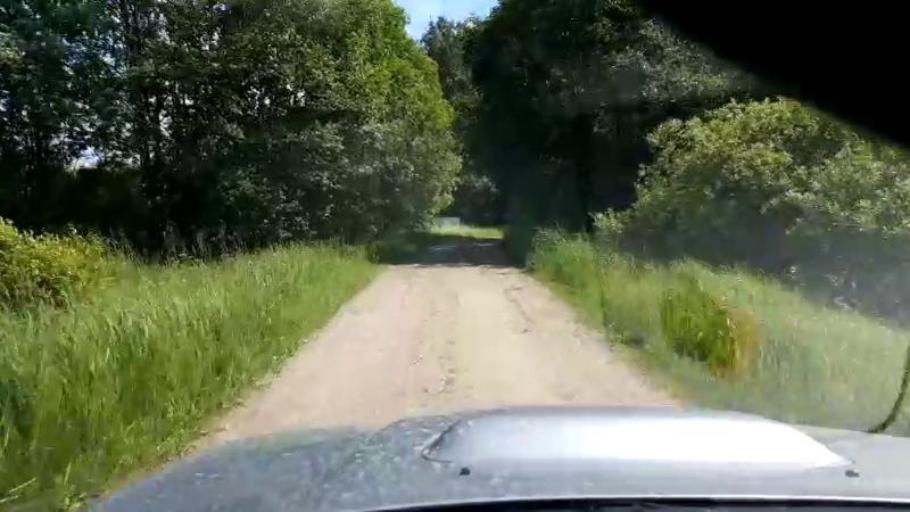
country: EE
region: Paernumaa
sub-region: Sindi linn
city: Sindi
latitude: 58.5326
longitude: 24.6643
